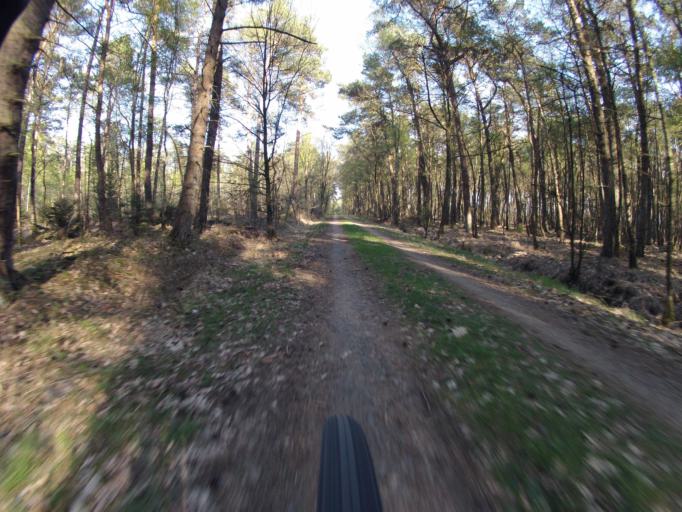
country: DE
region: Lower Saxony
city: Schuttorf
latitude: 52.3561
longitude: 7.2527
